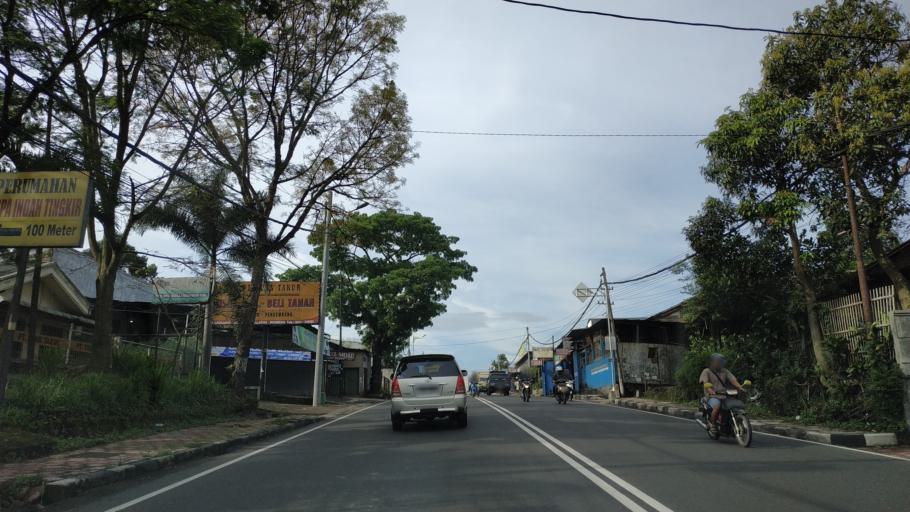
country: ID
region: Central Java
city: Salatiga
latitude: -7.3587
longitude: 110.5133
